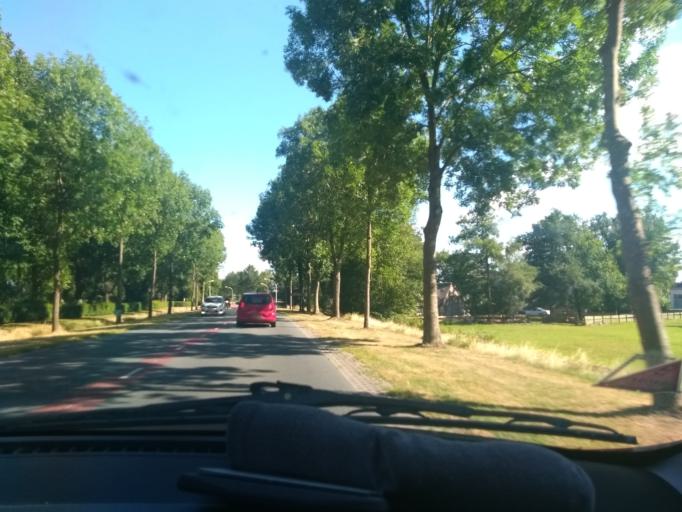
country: NL
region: Drenthe
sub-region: Gemeente Tynaarlo
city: Vries
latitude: 53.0966
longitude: 6.5473
